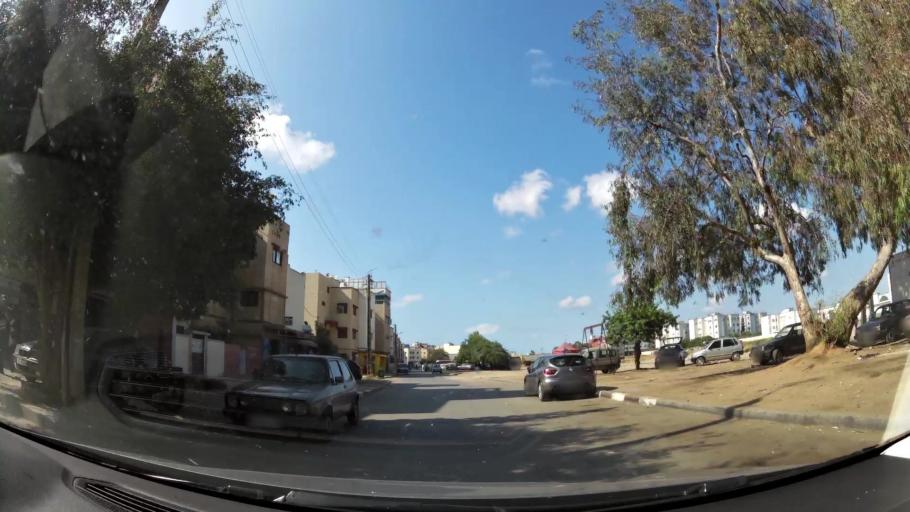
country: MA
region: Rabat-Sale-Zemmour-Zaer
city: Sale
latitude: 34.0445
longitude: -6.7772
